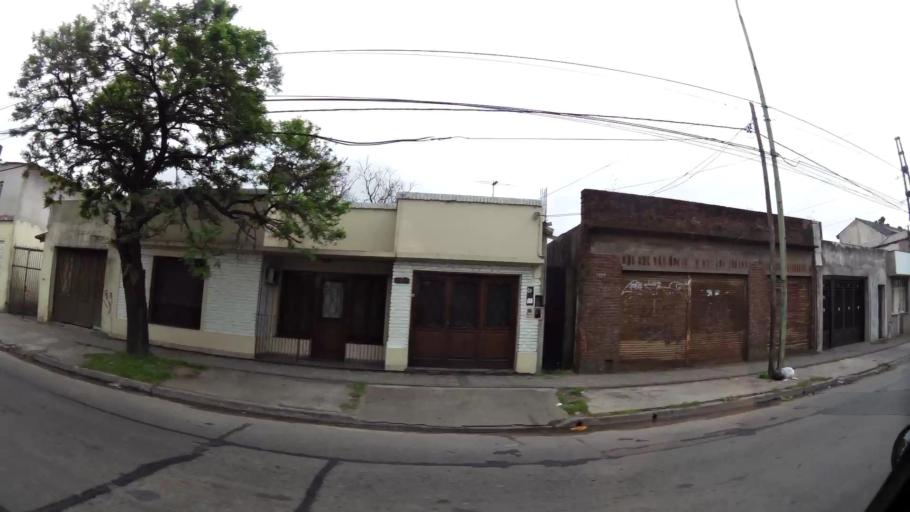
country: AR
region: Buenos Aires
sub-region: Partido de Quilmes
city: Quilmes
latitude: -34.7767
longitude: -58.2376
